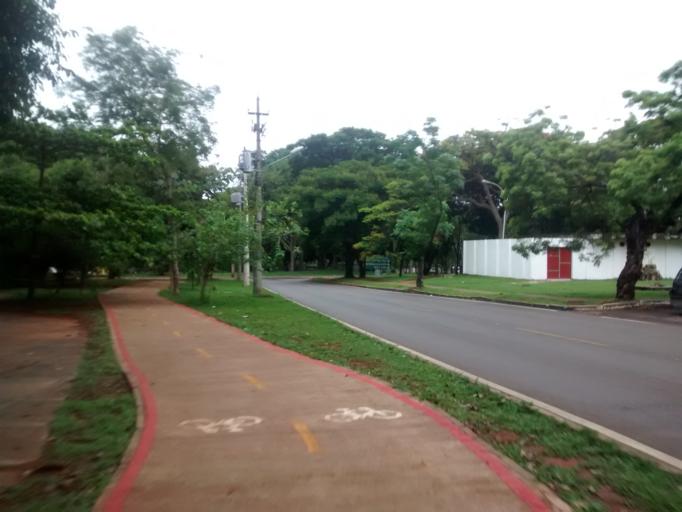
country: BR
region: Federal District
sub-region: Brasilia
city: Brasilia
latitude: -15.7643
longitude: -47.8722
